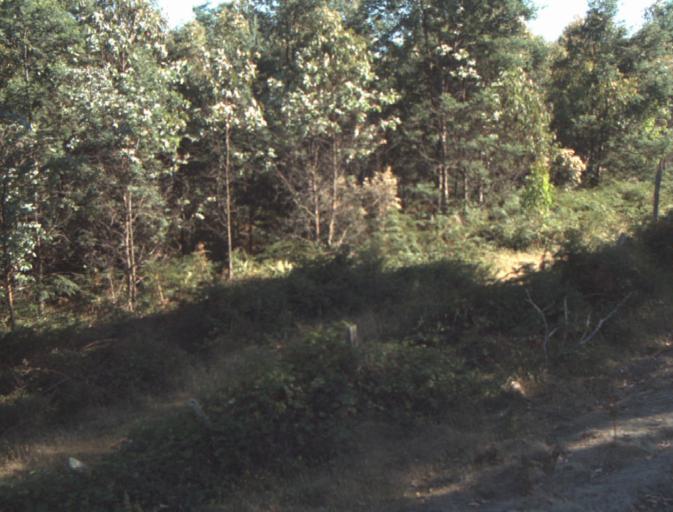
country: AU
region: Tasmania
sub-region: Dorset
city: Scottsdale
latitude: -41.2712
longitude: 147.3761
